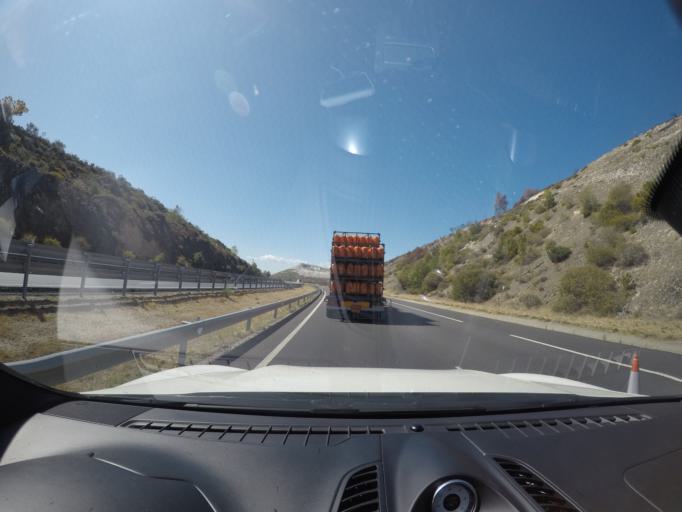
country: ES
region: Castille and Leon
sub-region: Provincia de Zamora
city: Pias
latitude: 42.0425
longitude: -7.0023
